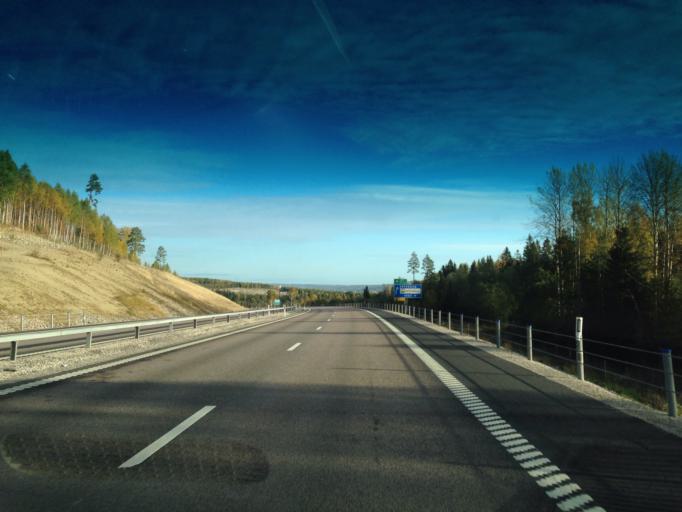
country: SE
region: Vaesternorrland
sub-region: Sundsvalls Kommun
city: Stockvik
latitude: 62.3251
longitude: 17.3440
